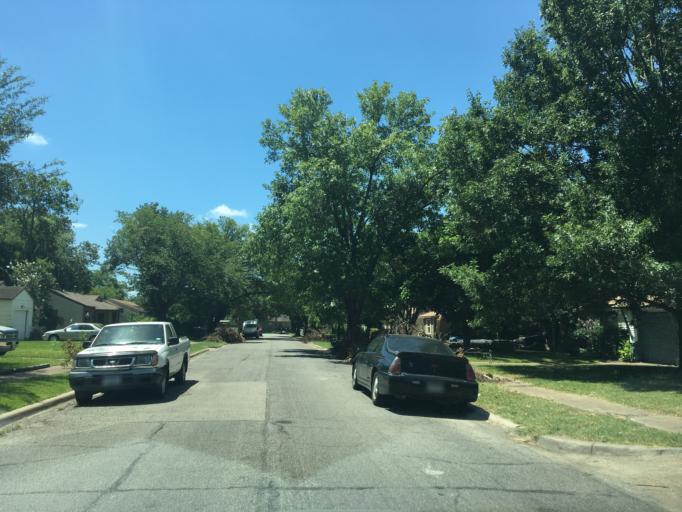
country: US
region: Texas
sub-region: Dallas County
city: Garland
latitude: 32.8407
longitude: -96.6782
